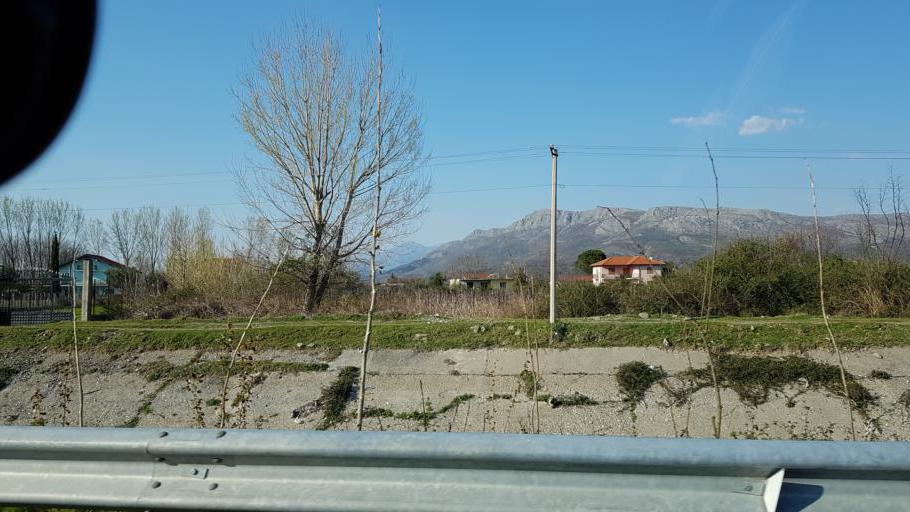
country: AL
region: Shkoder
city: Vukatane
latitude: 41.9906
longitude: 19.5762
